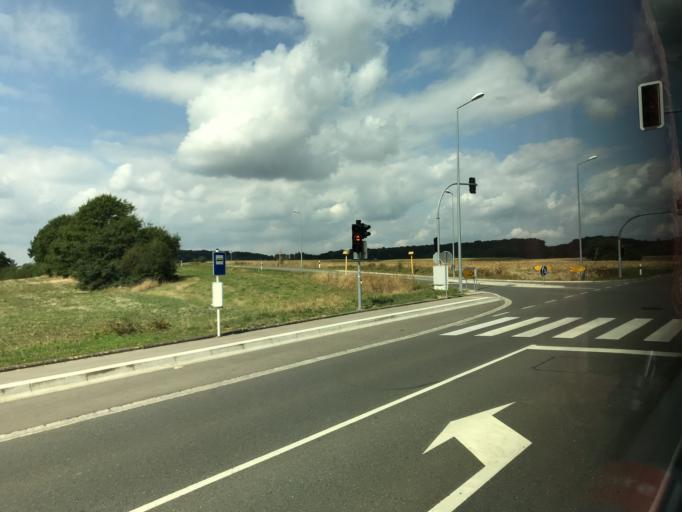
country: LU
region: Luxembourg
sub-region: Canton d'Esch-sur-Alzette
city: Frisange
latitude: 49.5334
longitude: 6.1797
